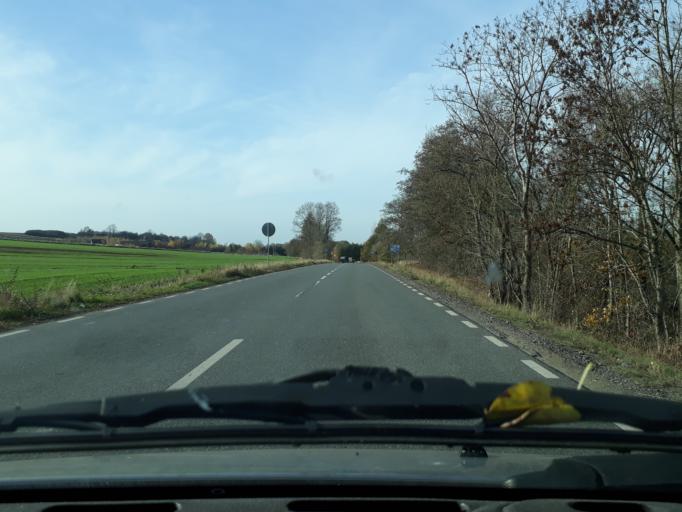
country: PL
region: Silesian Voivodeship
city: Wozniki
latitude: 50.5909
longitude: 19.0843
